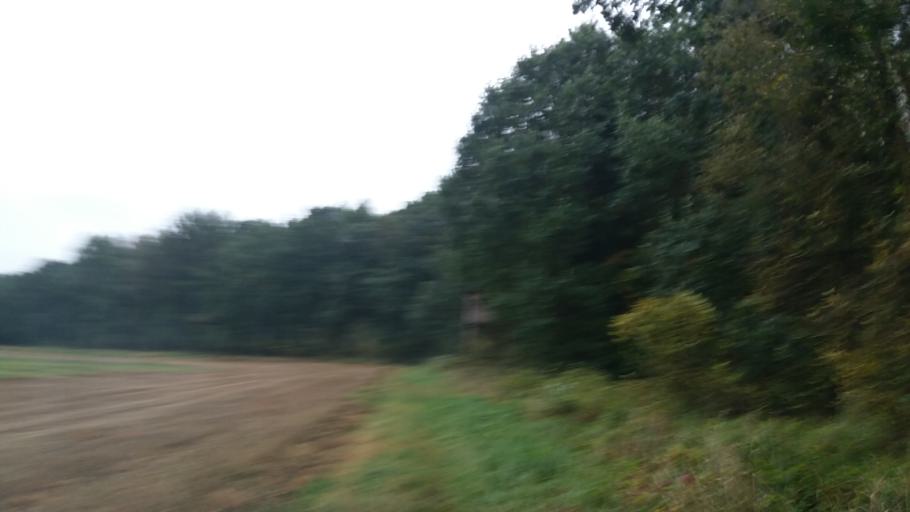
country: PL
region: West Pomeranian Voivodeship
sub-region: Powiat choszczenski
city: Pelczyce
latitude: 53.0709
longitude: 15.3002
